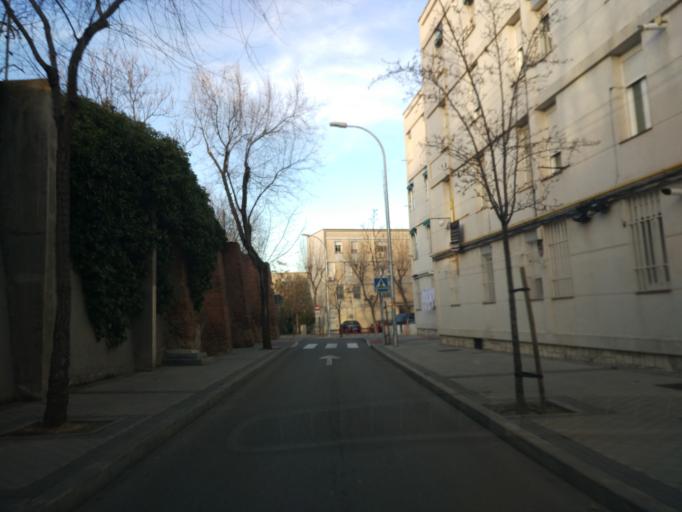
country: ES
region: Madrid
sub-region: Provincia de Madrid
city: Tetuan de las Victorias
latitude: 40.4610
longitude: -3.7143
